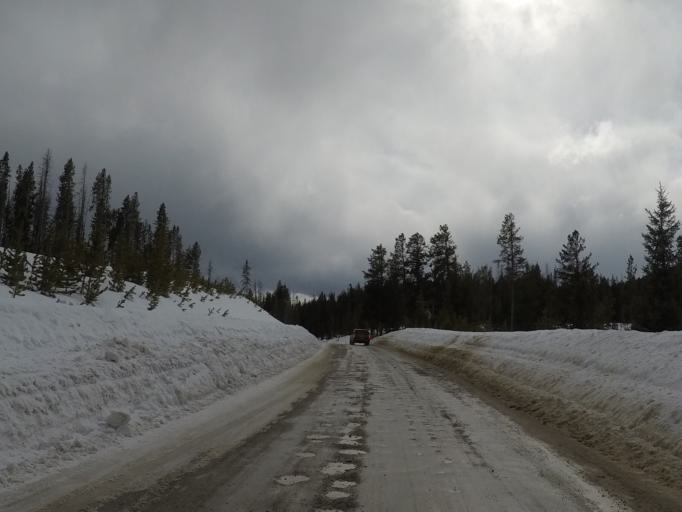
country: US
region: Montana
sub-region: Granite County
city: Philipsburg
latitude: 46.2284
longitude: -113.2492
